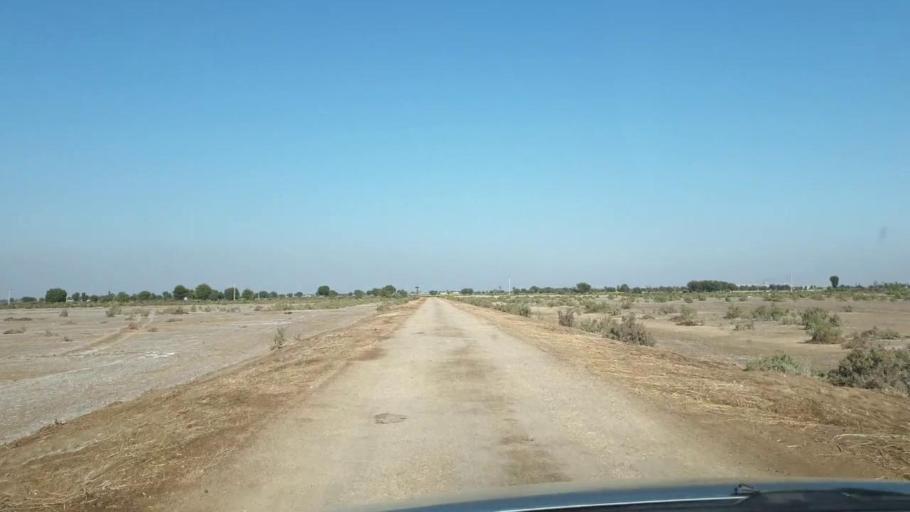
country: PK
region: Sindh
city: Jhol
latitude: 25.9178
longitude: 68.9847
